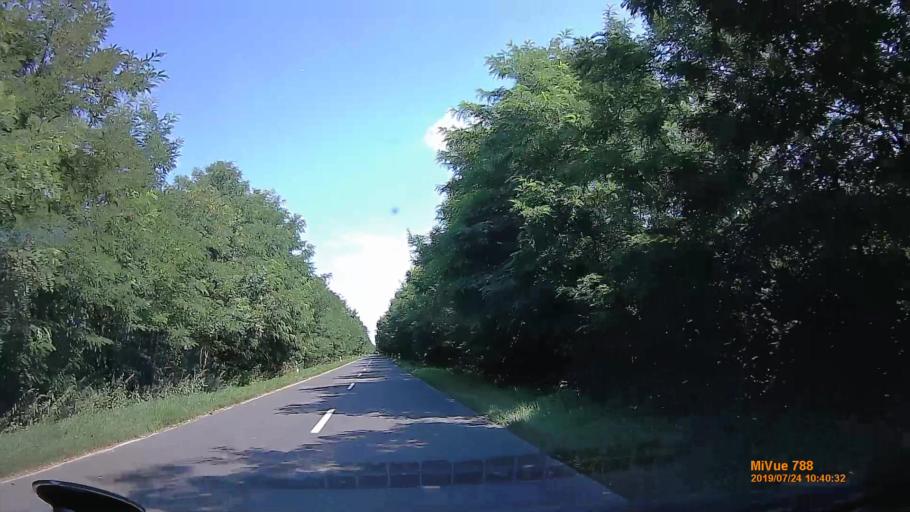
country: HU
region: Szabolcs-Szatmar-Bereg
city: Tarpa
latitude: 48.1764
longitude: 22.5460
